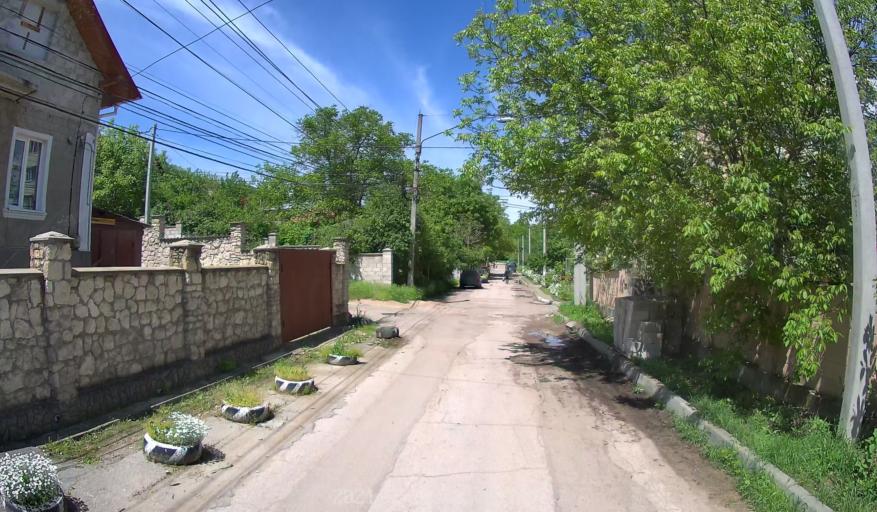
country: MD
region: Chisinau
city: Chisinau
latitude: 47.0530
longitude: 28.8315
